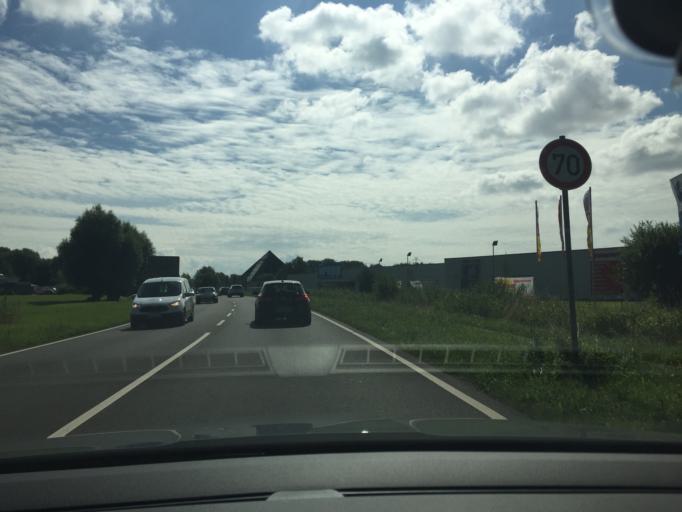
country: DE
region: Lower Saxony
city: Wilhelmshaven
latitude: 53.5233
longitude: 8.0744
